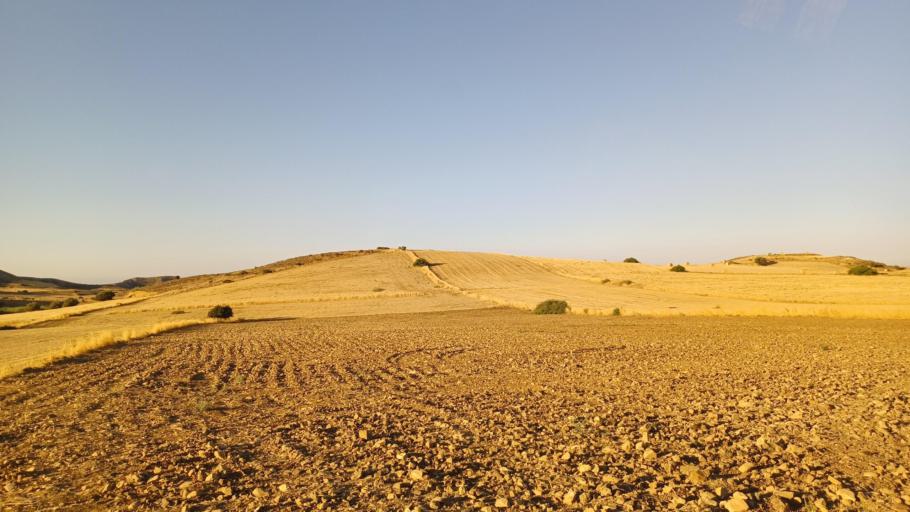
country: CY
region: Larnaka
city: Troulloi
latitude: 35.0317
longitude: 33.6453
